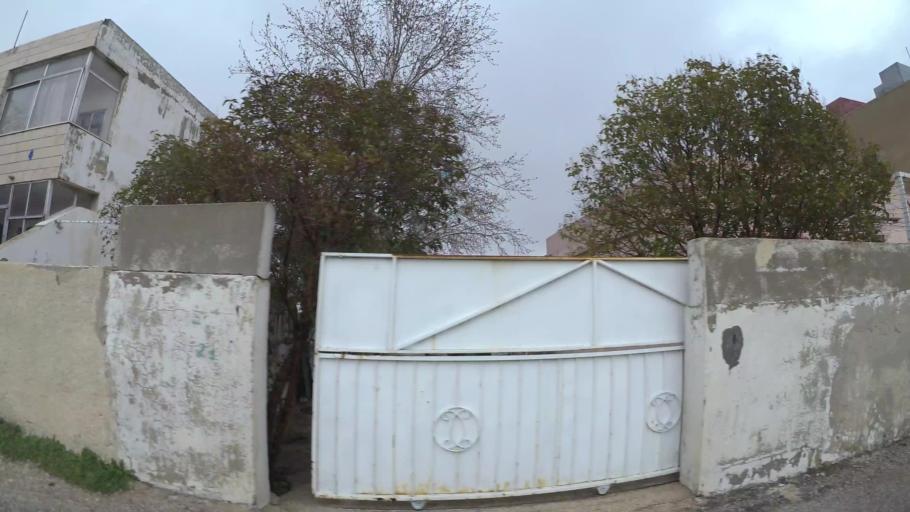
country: JO
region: Amman
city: Wadi as Sir
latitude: 31.9573
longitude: 35.8513
